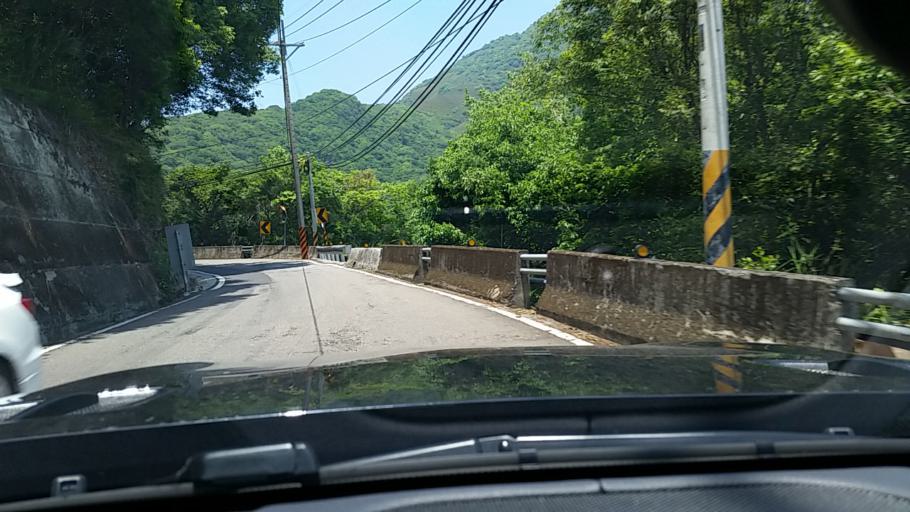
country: TW
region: Taiwan
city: Daxi
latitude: 24.6984
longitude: 121.3751
